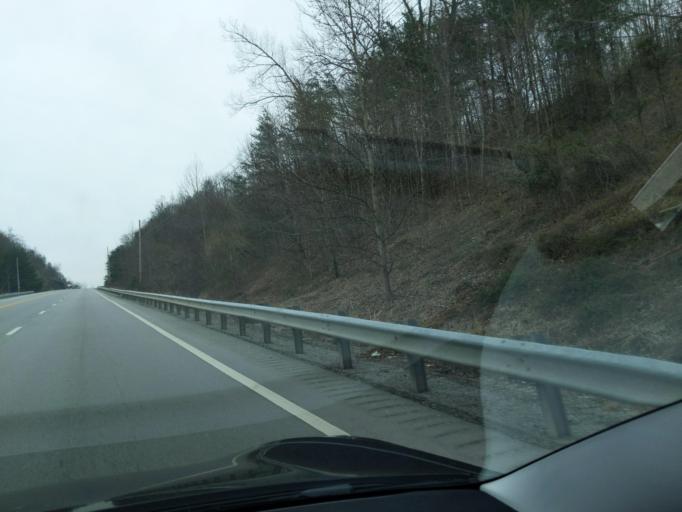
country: US
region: Kentucky
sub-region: Whitley County
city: Corbin
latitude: 36.9187
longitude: -84.1102
